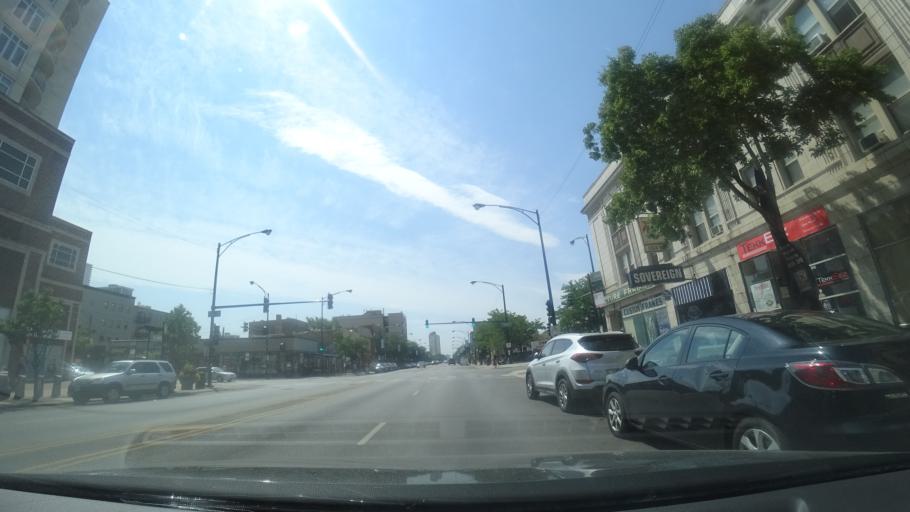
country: US
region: Illinois
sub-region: Cook County
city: Evanston
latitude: 41.9950
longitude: -87.6605
